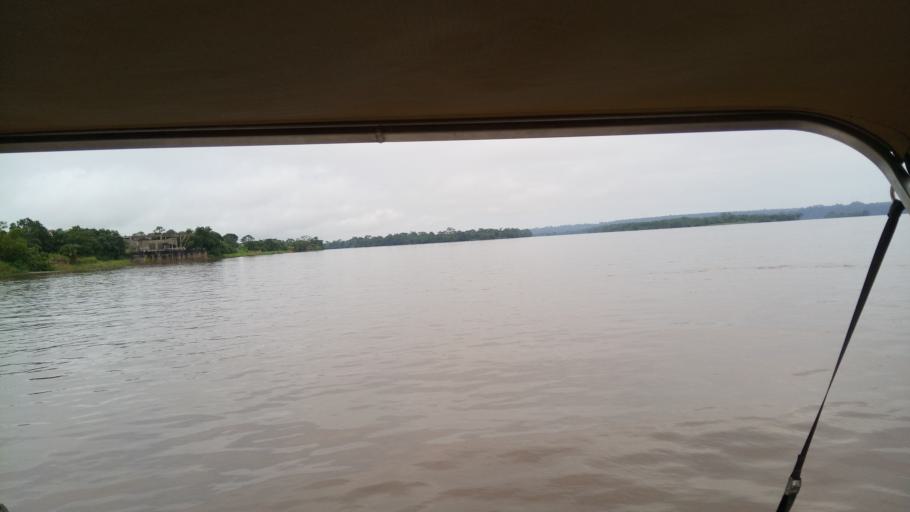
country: CD
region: Eastern Province
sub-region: Sous-Region de la Tshopo
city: Yangambi
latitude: 0.7144
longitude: 24.5615
